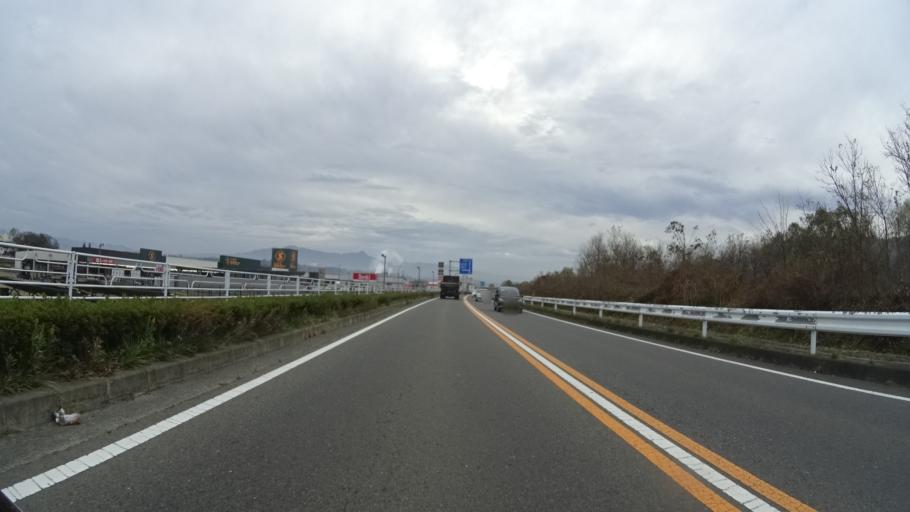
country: JP
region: Gunma
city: Numata
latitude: 36.6592
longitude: 139.0184
